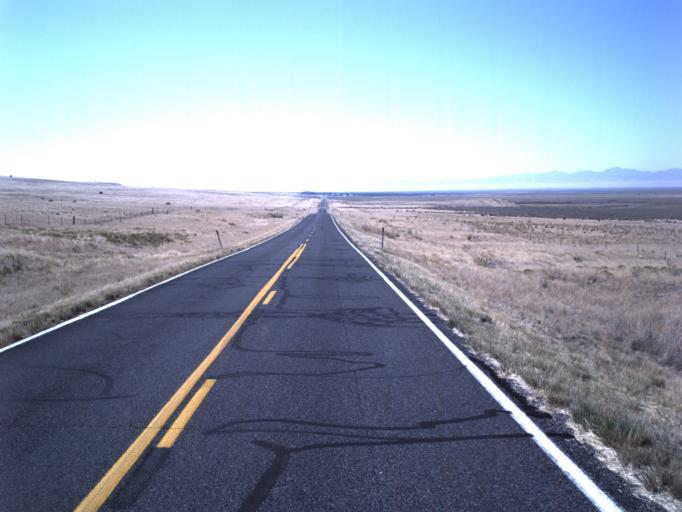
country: US
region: Utah
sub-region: Tooele County
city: Grantsville
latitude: 40.5784
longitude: -112.7267
